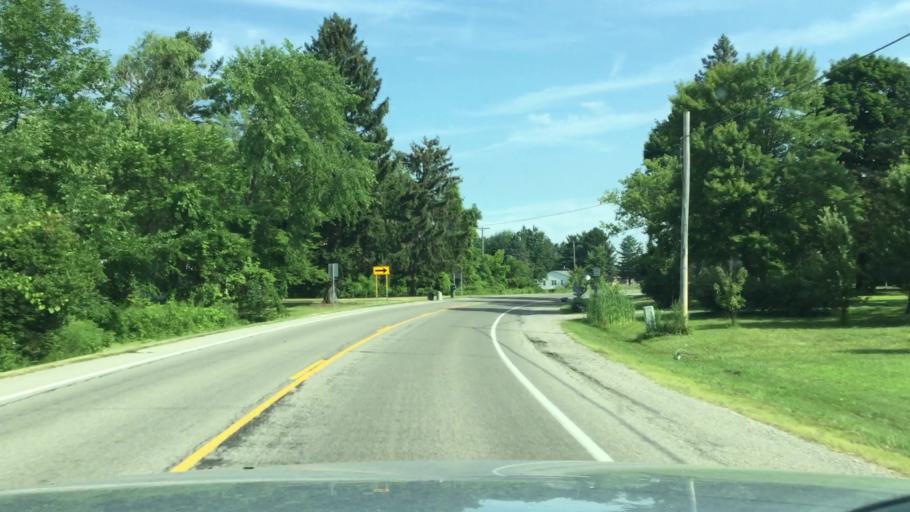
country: US
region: Michigan
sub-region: Genesee County
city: Flushing
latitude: 43.1073
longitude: -83.8725
